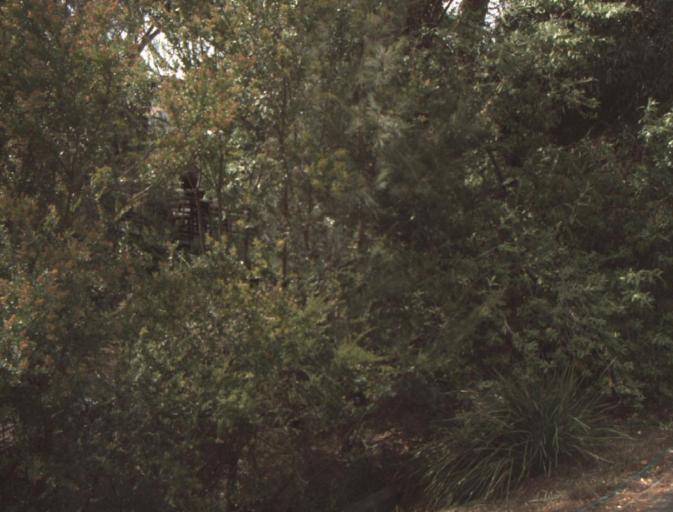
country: AU
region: Tasmania
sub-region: Launceston
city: East Launceston
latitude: -41.4416
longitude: 147.1490
